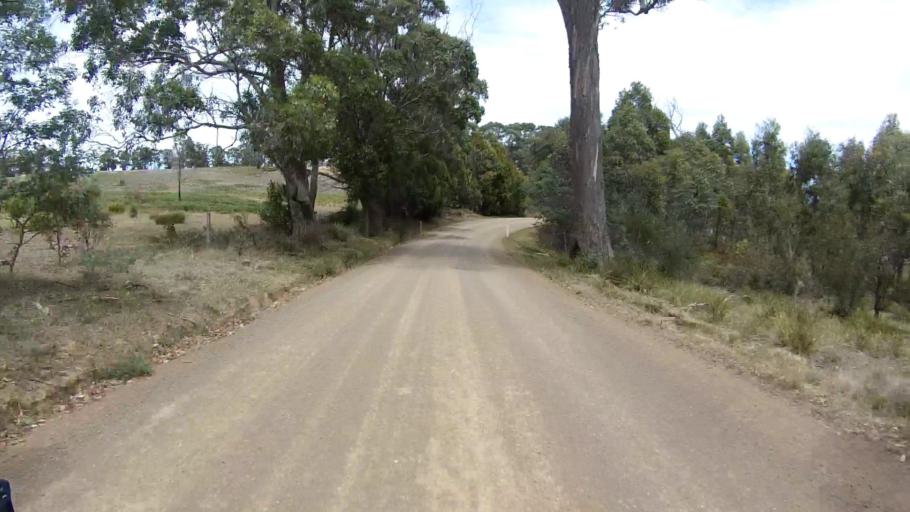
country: AU
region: Tasmania
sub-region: Sorell
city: Sorell
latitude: -42.7919
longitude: 147.6963
